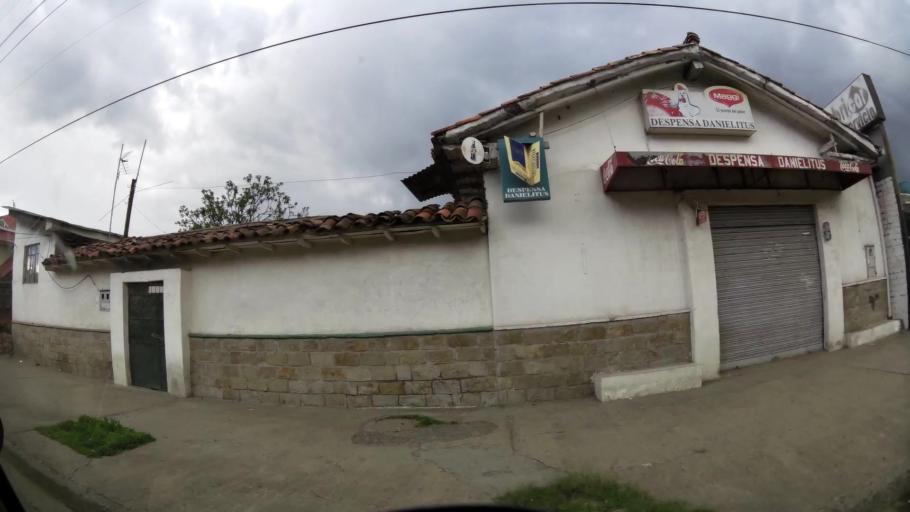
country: EC
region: Azuay
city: Cuenca
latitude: -2.8890
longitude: -79.0197
